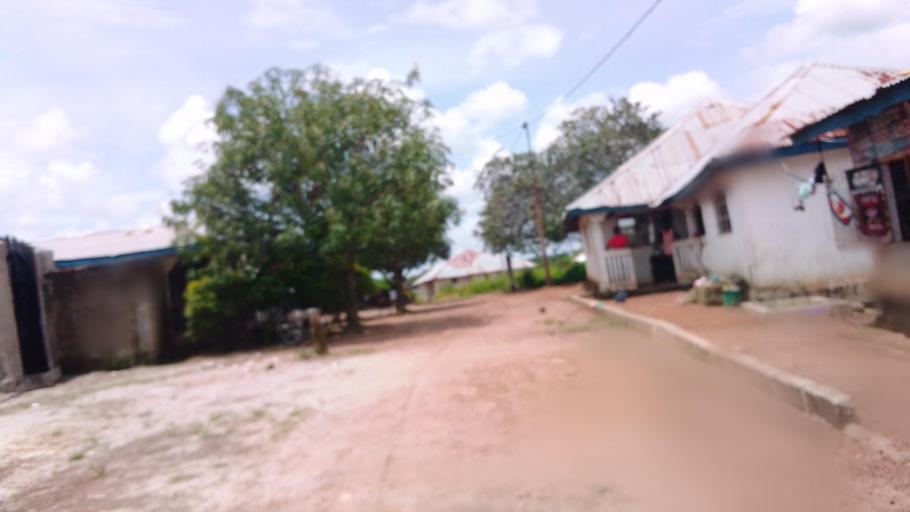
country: SL
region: Northern Province
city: Makeni
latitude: 8.8637
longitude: -12.0374
